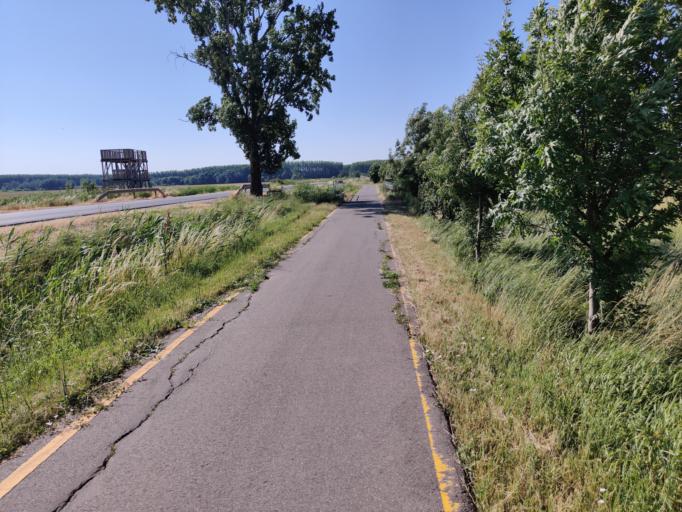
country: HU
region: Hajdu-Bihar
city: Balmazujvaros
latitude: 47.5910
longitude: 21.3426
